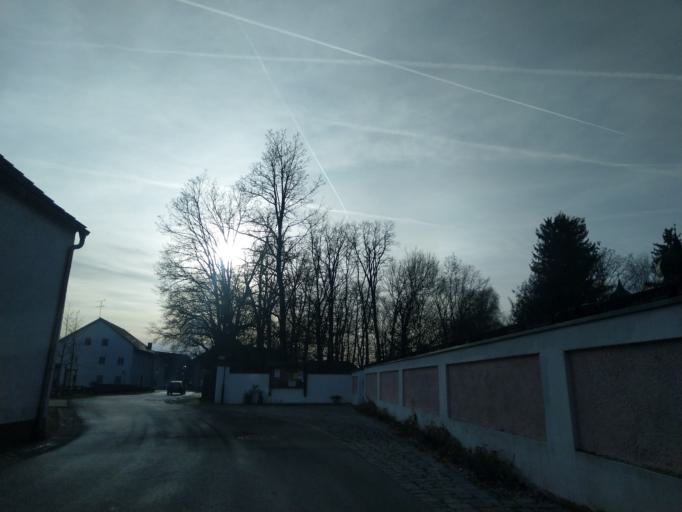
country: DE
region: Bavaria
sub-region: Lower Bavaria
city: Oberporing
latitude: 48.7127
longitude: 12.8411
